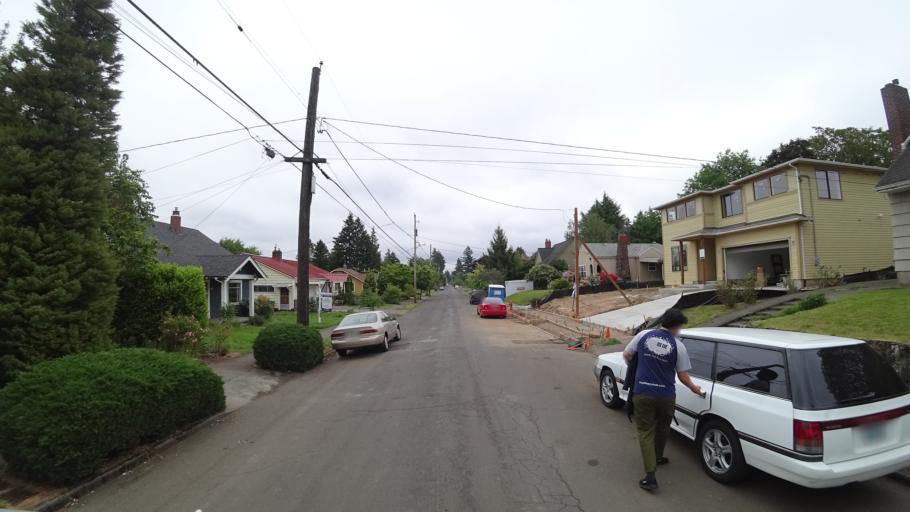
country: US
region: Oregon
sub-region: Multnomah County
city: Portland
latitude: 45.5546
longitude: -122.6180
